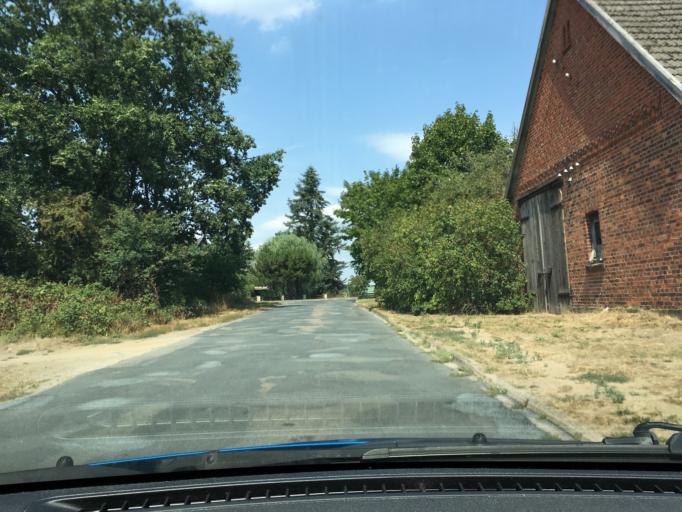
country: DE
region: Lower Saxony
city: Barnstedt
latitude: 53.1250
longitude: 10.4242
